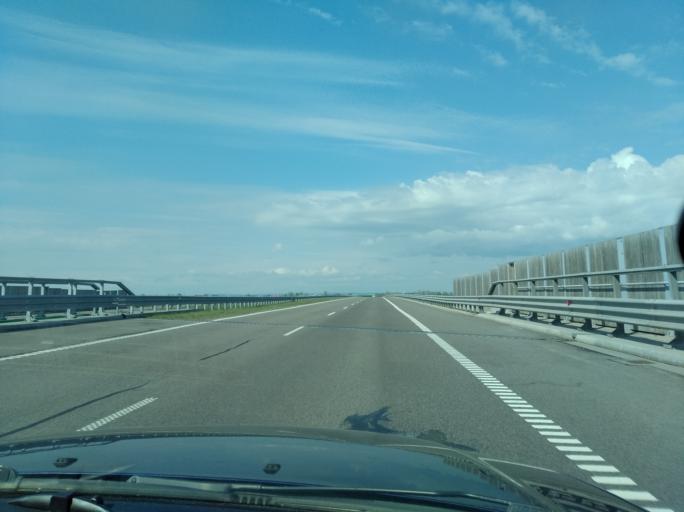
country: PL
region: Subcarpathian Voivodeship
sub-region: Powiat jaroslawski
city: Sosnica
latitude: 49.9299
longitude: 22.9129
